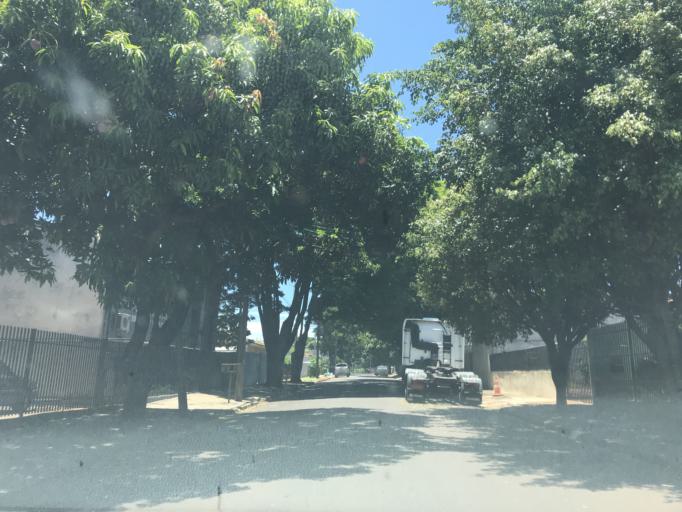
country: BR
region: Parana
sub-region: Sarandi
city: Sarandi
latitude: -23.4389
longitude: -51.8954
